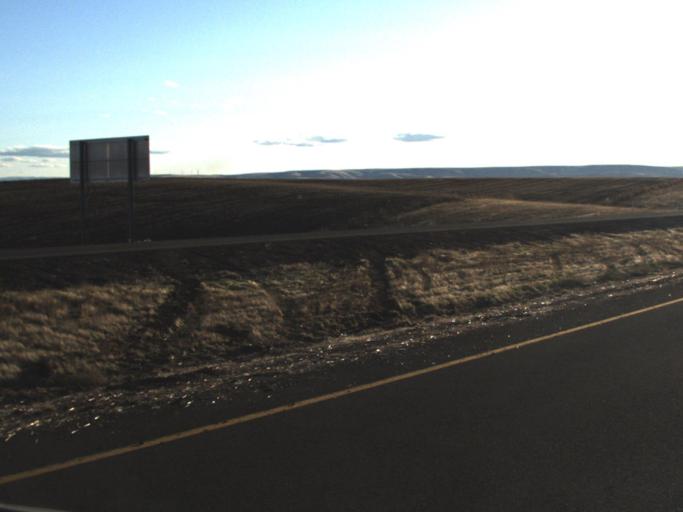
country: US
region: Washington
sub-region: Walla Walla County
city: Garrett
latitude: 46.0690
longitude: -118.4206
